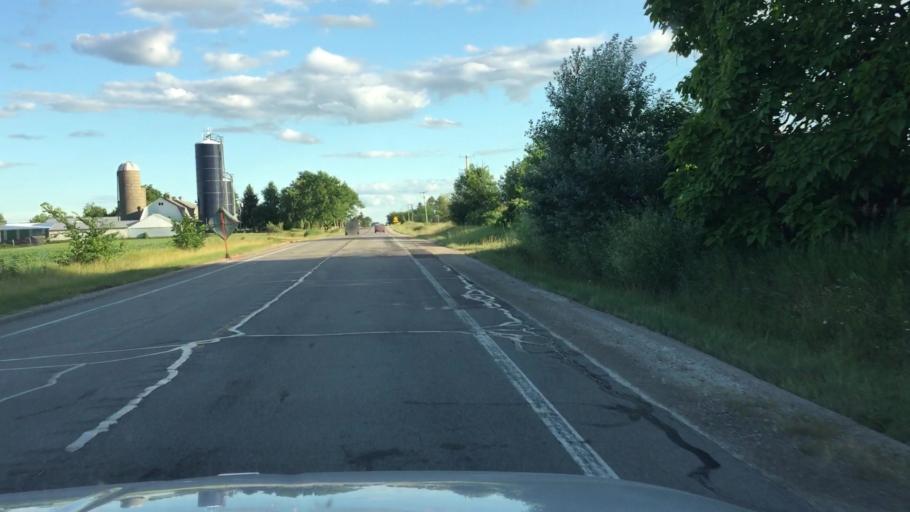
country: US
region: Michigan
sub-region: Saint Clair County
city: Yale
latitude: 43.0921
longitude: -82.7664
